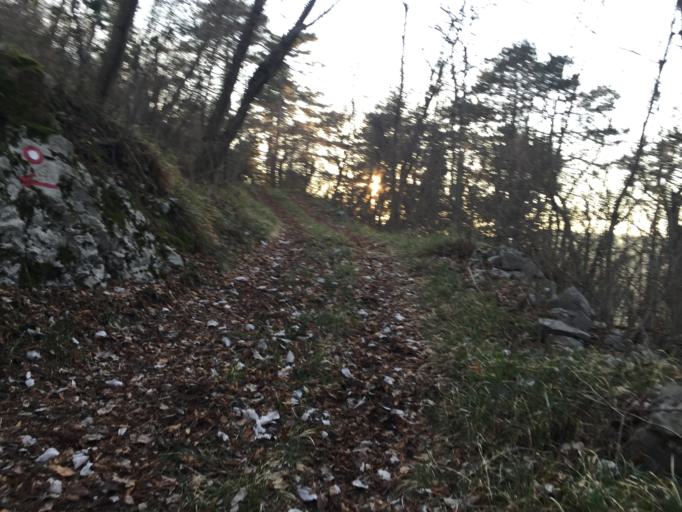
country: SI
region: Kanal
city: Kanal
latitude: 46.0427
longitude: 13.6743
